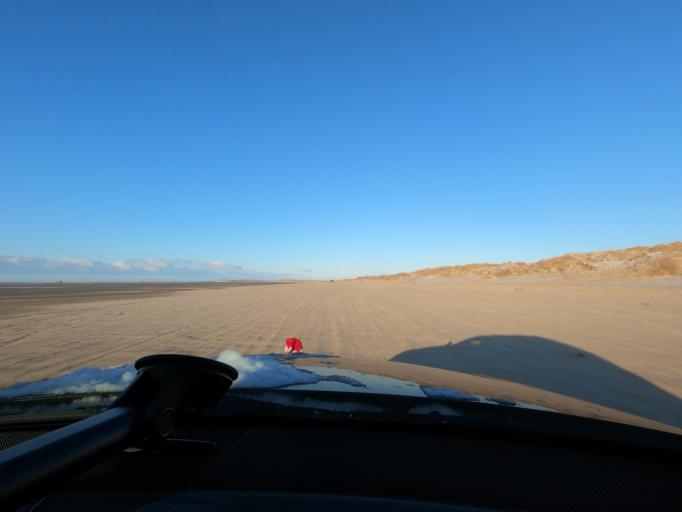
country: DE
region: Schleswig-Holstein
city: List
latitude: 55.1467
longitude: 8.4873
